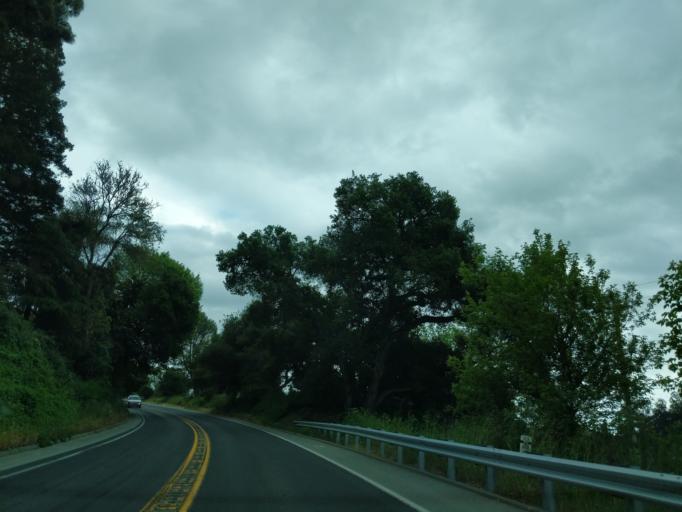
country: US
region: California
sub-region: San Benito County
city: Aromas
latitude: 36.9077
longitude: -121.6509
